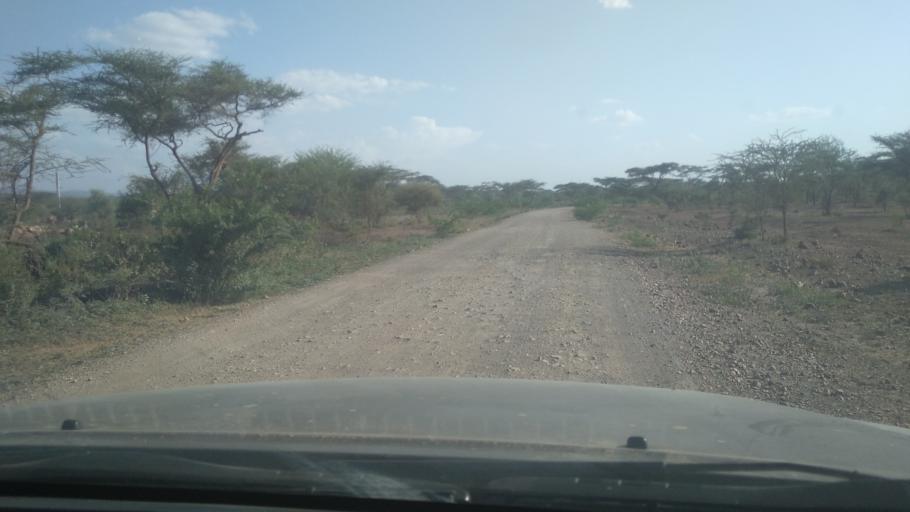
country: ET
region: Oromiya
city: Hirna
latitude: 9.4830
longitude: 41.0161
